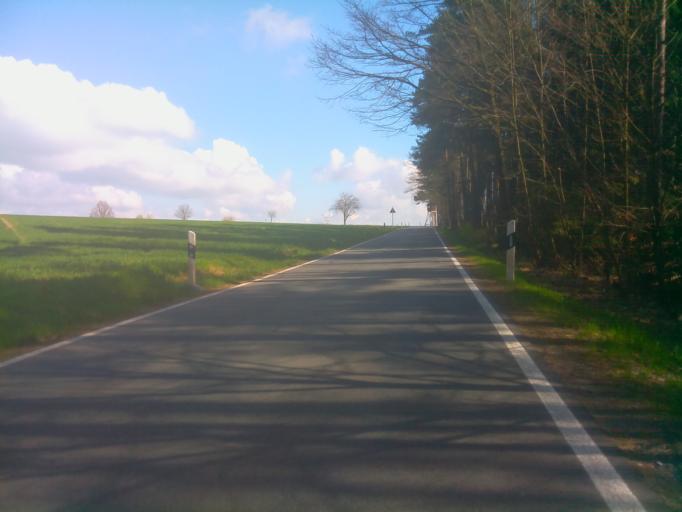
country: DE
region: Thuringia
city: Oberbodnitz
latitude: 50.7787
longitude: 11.6761
